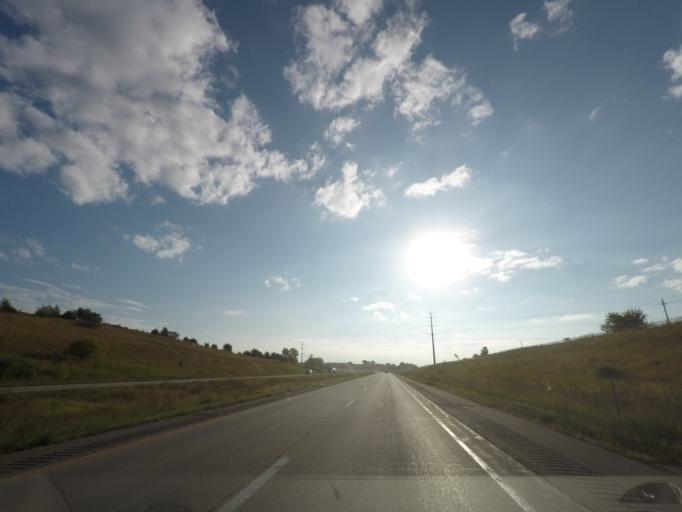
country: US
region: Iowa
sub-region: Warren County
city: Norwalk
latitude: 41.4981
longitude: -93.6144
